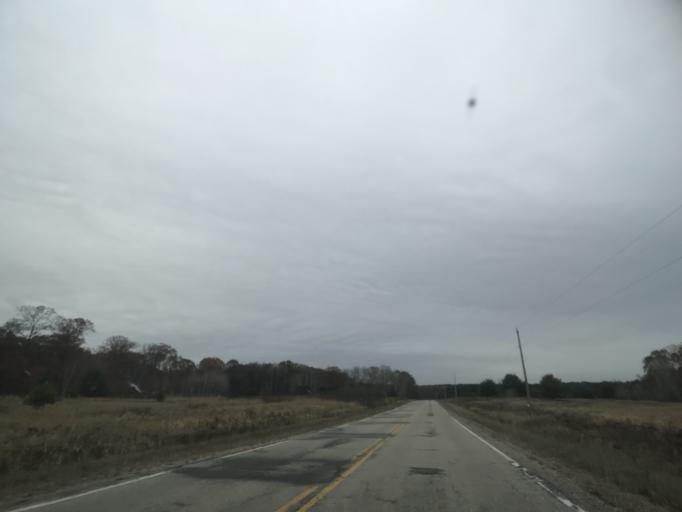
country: US
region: Wisconsin
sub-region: Oconto County
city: Gillett
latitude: 45.3834
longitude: -88.3595
